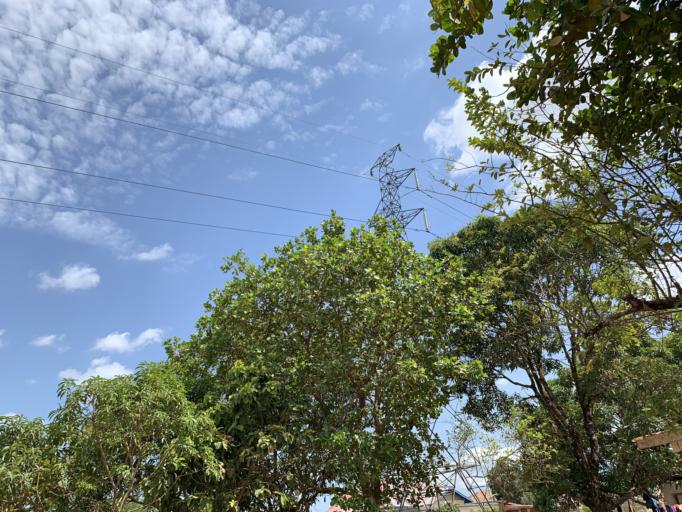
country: SL
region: Western Area
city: Waterloo
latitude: 8.3276
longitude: -13.0393
